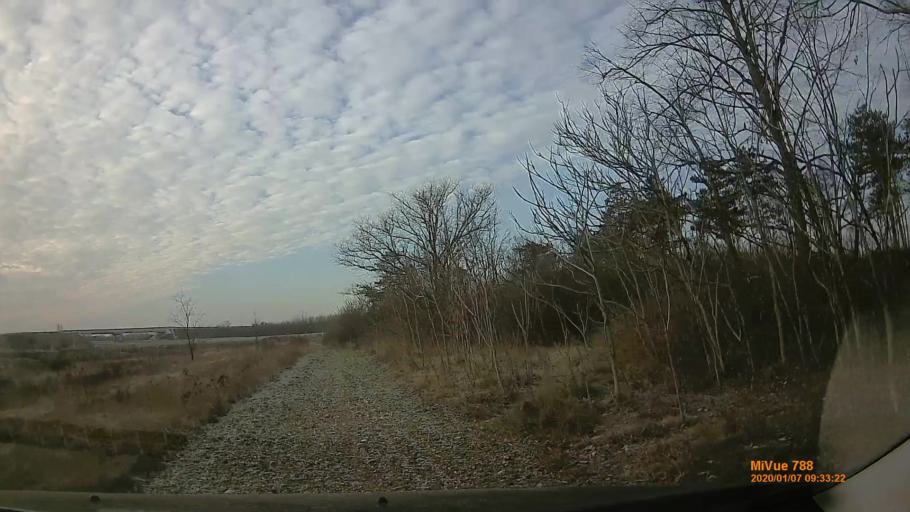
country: HU
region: Gyor-Moson-Sopron
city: Rajka
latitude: 47.9430
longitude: 17.1683
